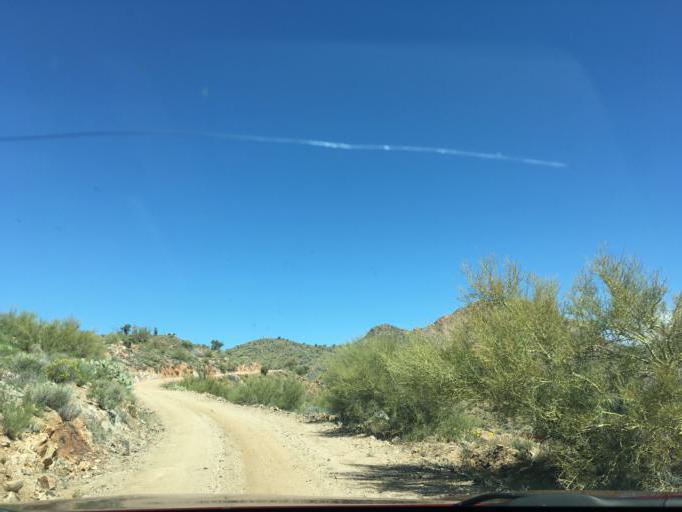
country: US
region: Arizona
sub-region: Yavapai County
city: Bagdad
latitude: 34.6081
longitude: -113.3989
